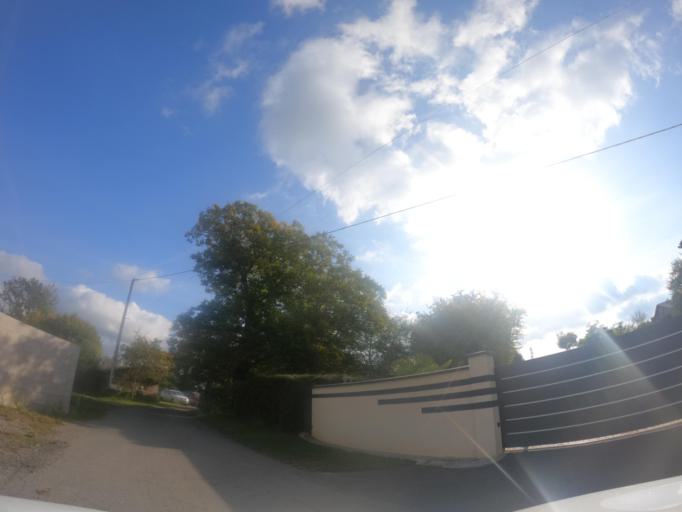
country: FR
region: Poitou-Charentes
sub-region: Departement des Deux-Sevres
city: La Foret-sur-Sevre
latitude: 46.7820
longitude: -0.6151
